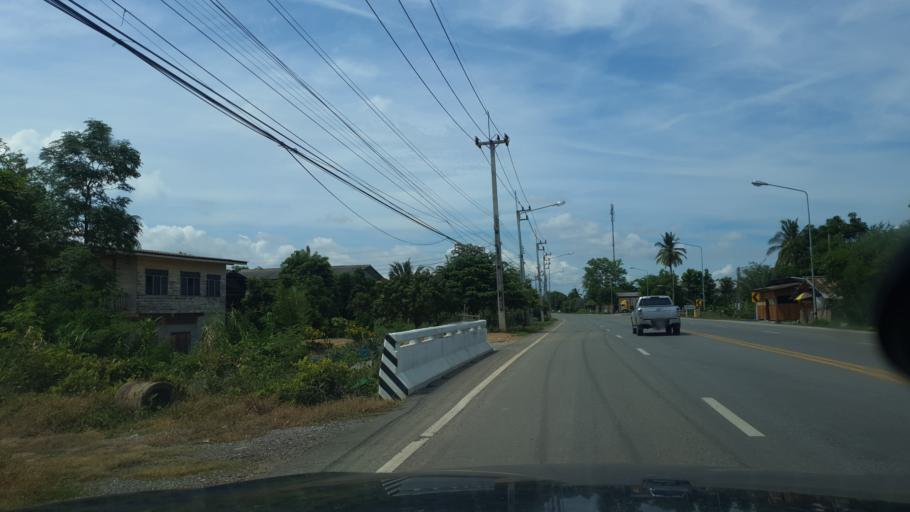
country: TH
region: Sukhothai
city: Sukhothai
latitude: 17.0472
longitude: 99.8161
